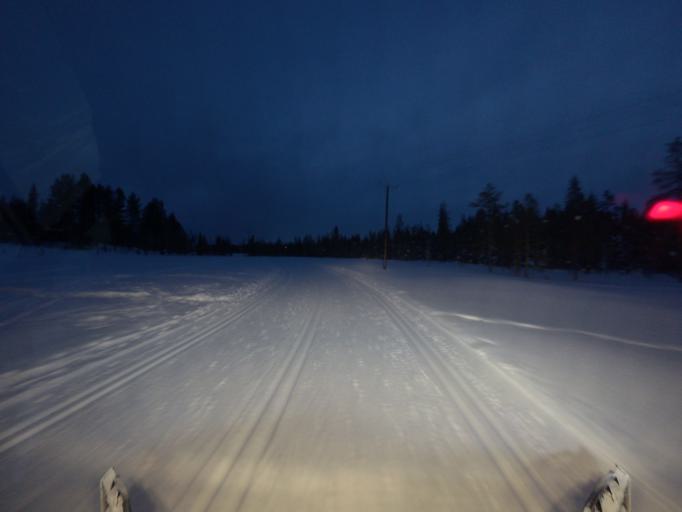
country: FI
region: Lapland
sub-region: Tunturi-Lappi
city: Kolari
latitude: 67.6042
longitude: 24.1354
